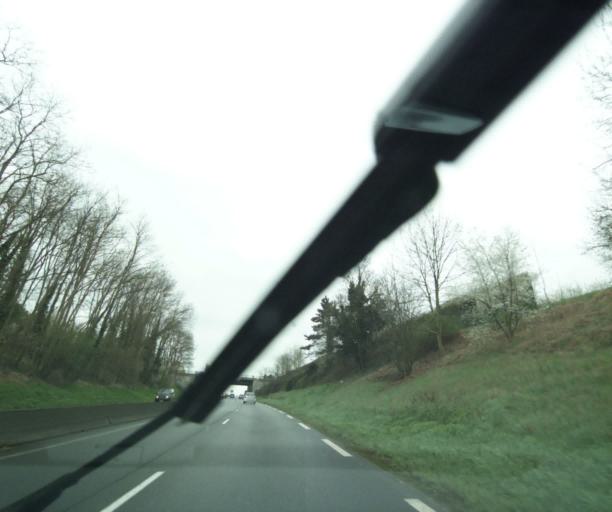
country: FR
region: Ile-de-France
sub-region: Departement de l'Essonne
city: Egly
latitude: 48.5844
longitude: 2.2338
